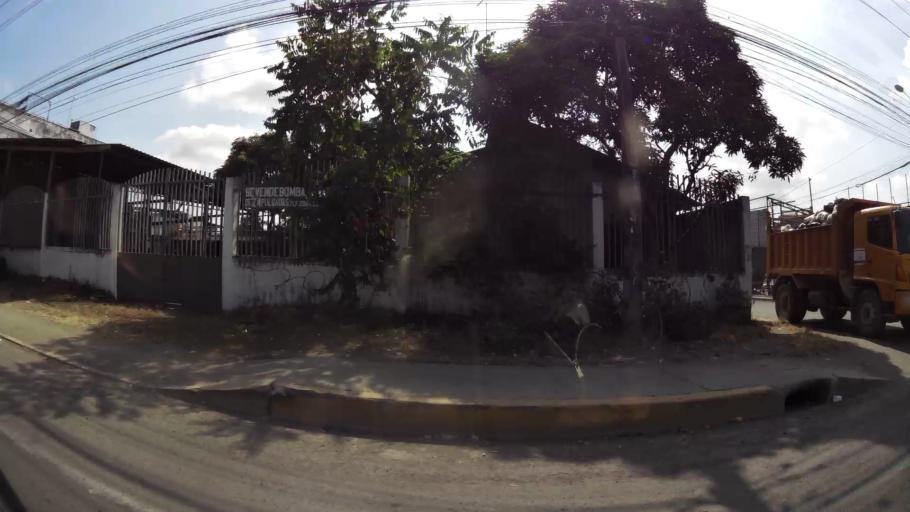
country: EC
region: Guayas
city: Eloy Alfaro
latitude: -2.1760
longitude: -79.8291
